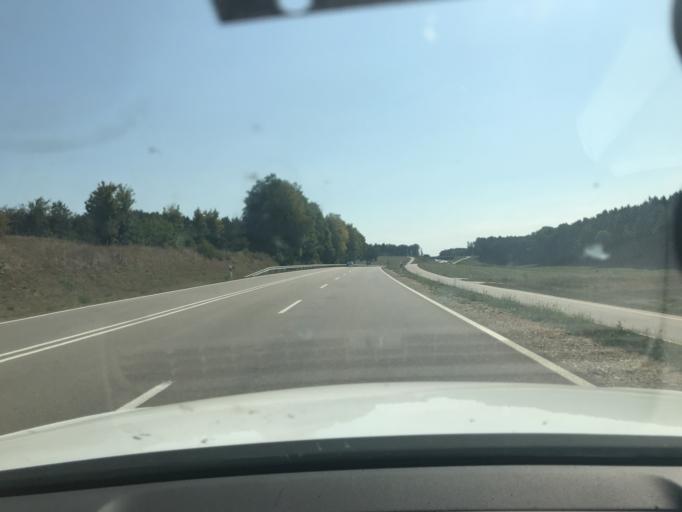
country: DE
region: Bavaria
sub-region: Upper Palatinate
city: Poppenricht
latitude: 49.4623
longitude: 11.7950
